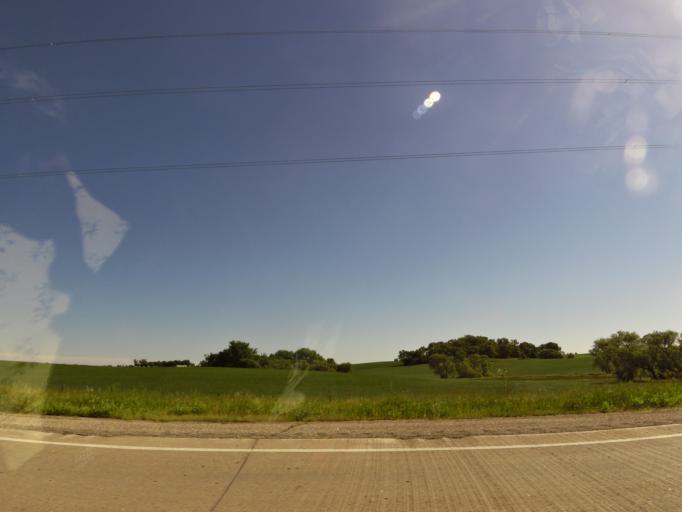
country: US
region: Minnesota
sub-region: Otter Tail County
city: Pelican Rapids
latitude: 46.4762
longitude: -96.2674
